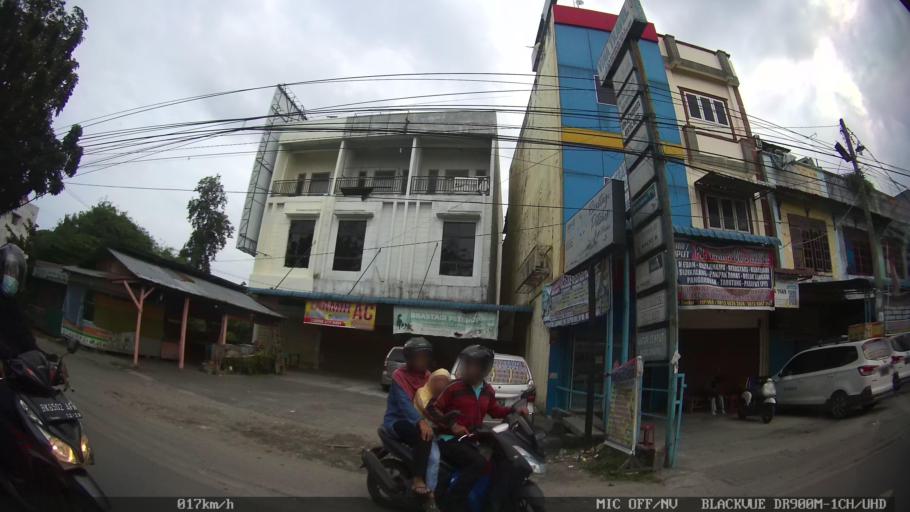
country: ID
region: North Sumatra
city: Deli Tua
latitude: 3.5412
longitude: 98.6612
